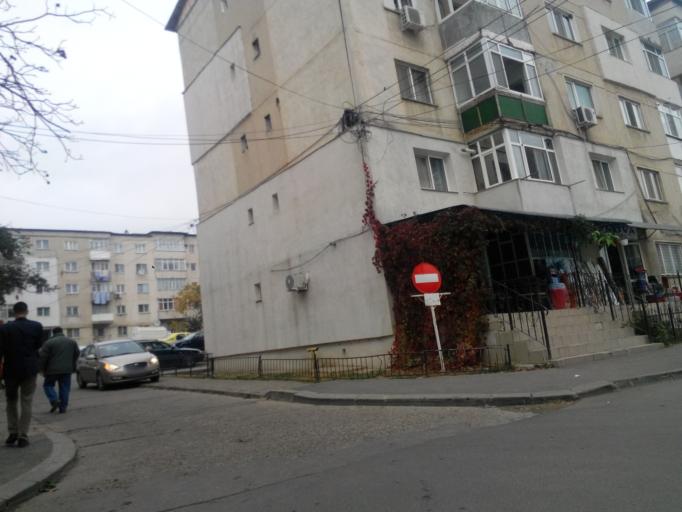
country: RO
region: Vaslui
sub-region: Municipiul Husi
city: Husi
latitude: 46.6746
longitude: 28.0620
